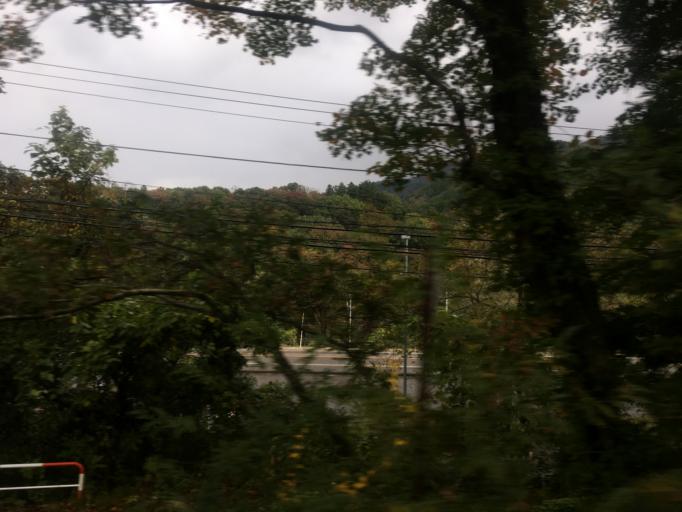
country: JP
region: Niigata
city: Murakami
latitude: 38.0674
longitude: 139.6002
